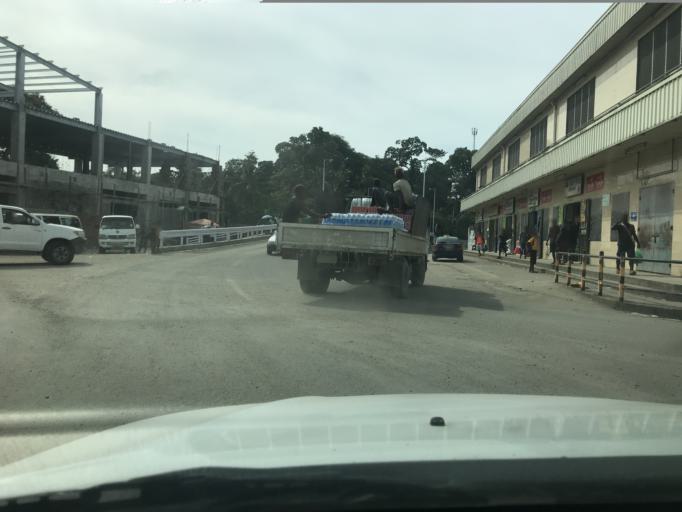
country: SB
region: Guadalcanal
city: Honiara
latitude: -9.4393
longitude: 159.9642
